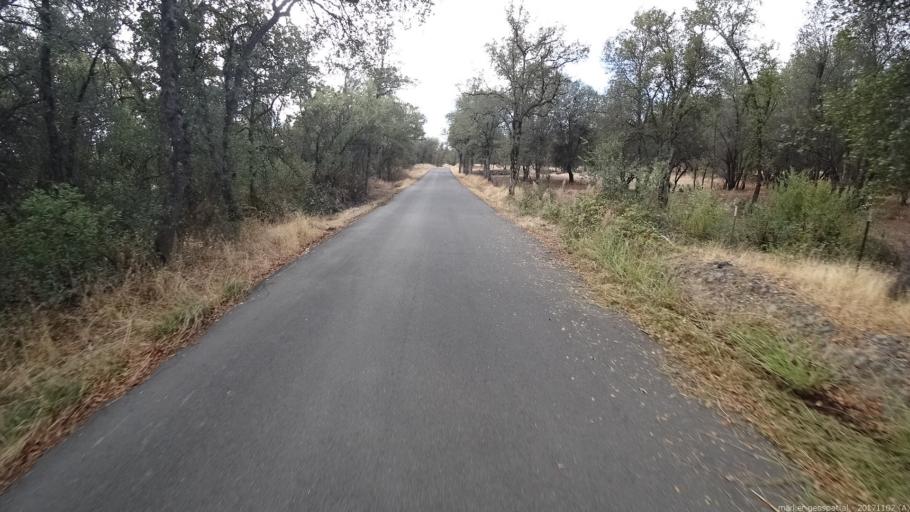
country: US
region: California
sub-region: Shasta County
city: Shasta
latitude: 40.5086
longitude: -122.5712
